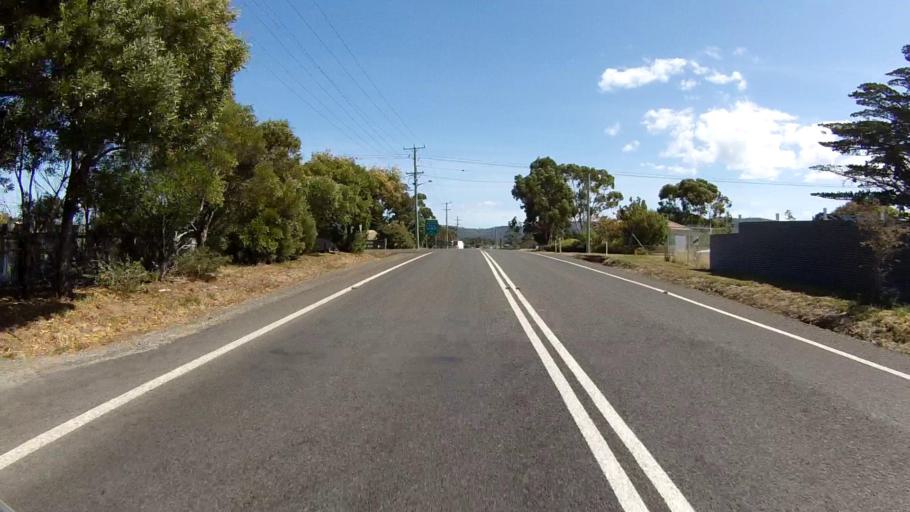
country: AU
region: Tasmania
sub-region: Sorell
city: Sorell
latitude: -42.5006
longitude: 147.9181
